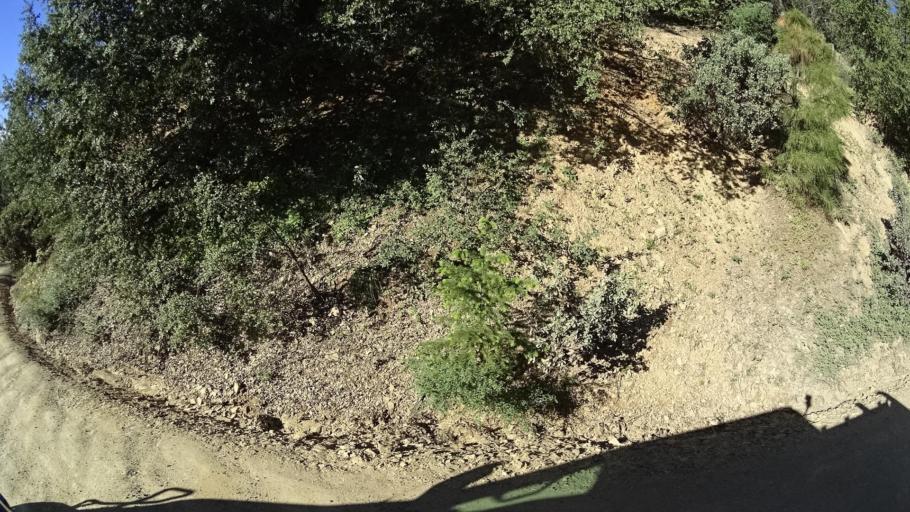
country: US
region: California
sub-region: Lake County
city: Upper Lake
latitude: 39.3183
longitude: -122.9458
